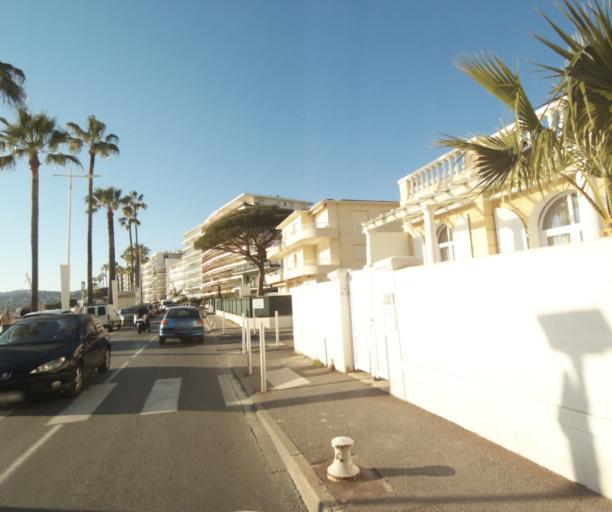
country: FR
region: Provence-Alpes-Cote d'Azur
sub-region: Departement des Alpes-Maritimes
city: Antibes
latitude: 43.5701
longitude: 7.1058
